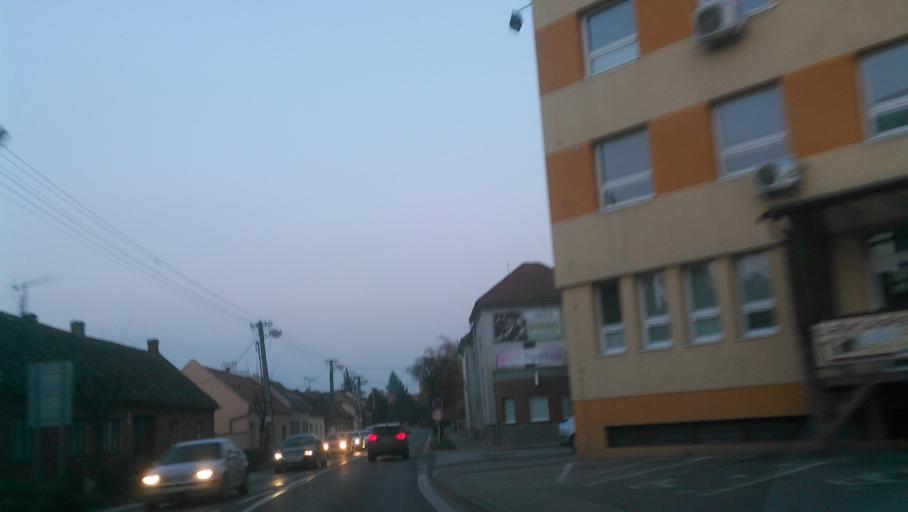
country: SK
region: Bratislavsky
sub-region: Okres Pezinok
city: Pezinok
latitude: 48.2856
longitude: 17.2730
